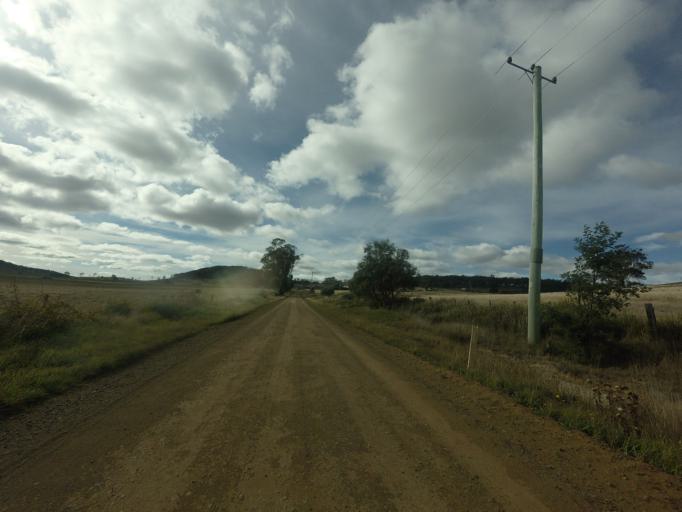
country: AU
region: Tasmania
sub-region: Brighton
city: Bridgewater
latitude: -42.3946
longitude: 147.3955
